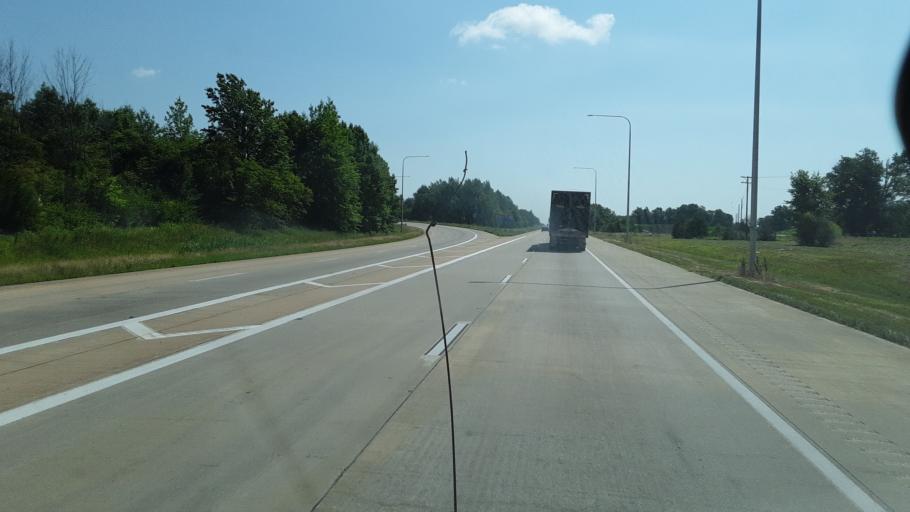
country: US
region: Illinois
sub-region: Effingham County
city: Effingham
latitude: 39.1482
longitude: -88.5124
